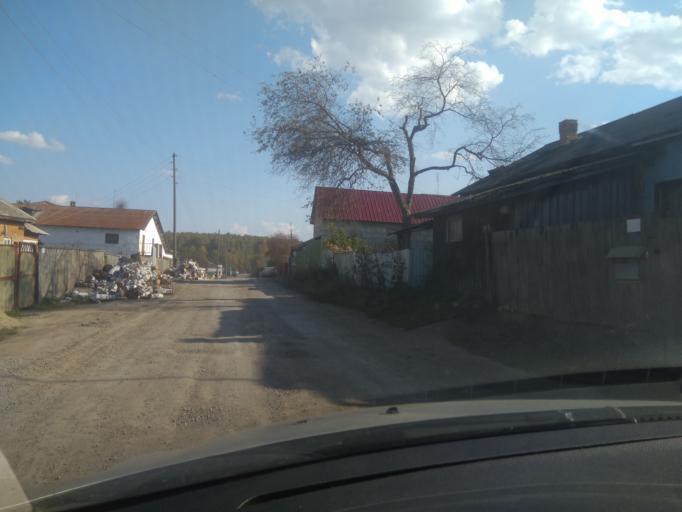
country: RU
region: Sverdlovsk
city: Pokrovskoye
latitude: 56.4344
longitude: 61.5909
